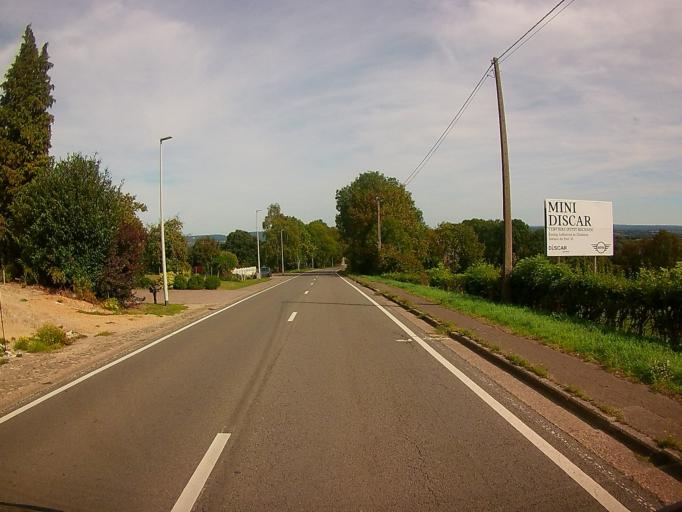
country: BE
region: Wallonia
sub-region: Province de Liege
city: Welkenraedt
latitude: 50.6806
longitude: 5.9412
